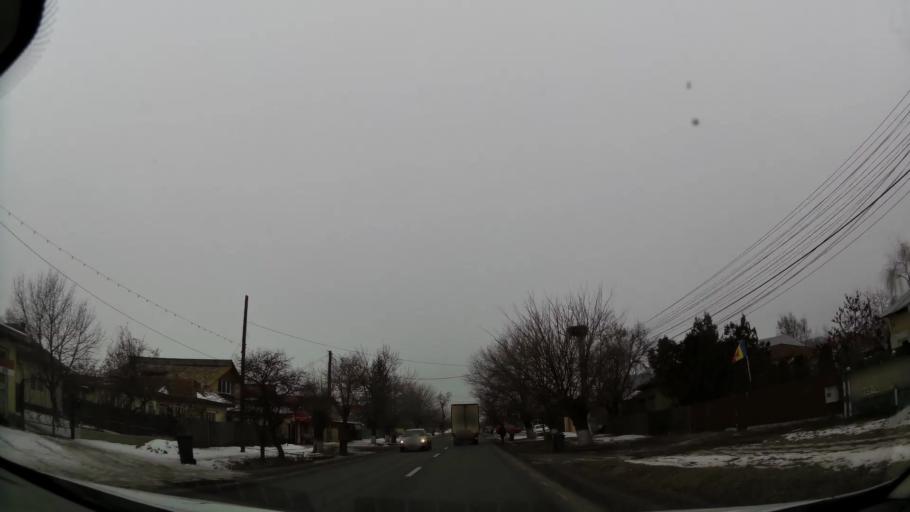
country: RO
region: Dambovita
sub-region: Comuna Tartasesti
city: Baldana
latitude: 44.6167
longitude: 25.7608
